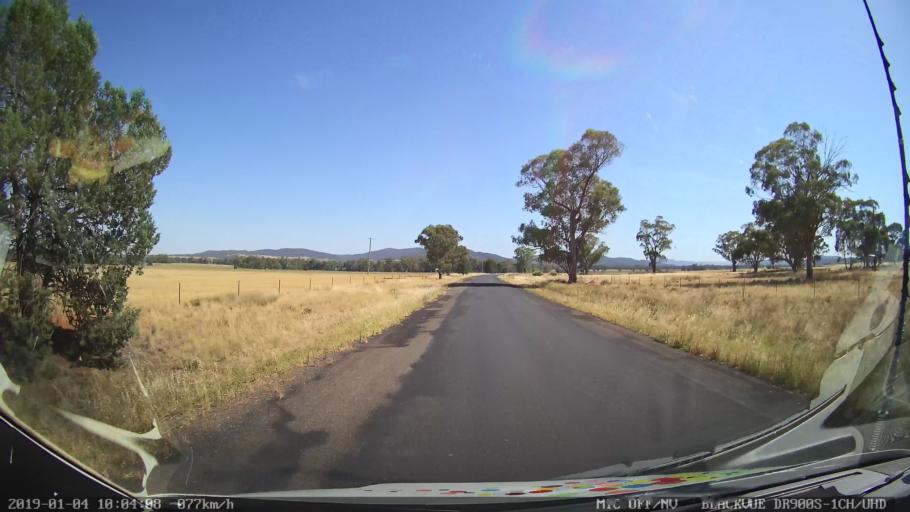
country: AU
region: New South Wales
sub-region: Cabonne
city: Canowindra
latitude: -33.4559
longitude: 148.3611
